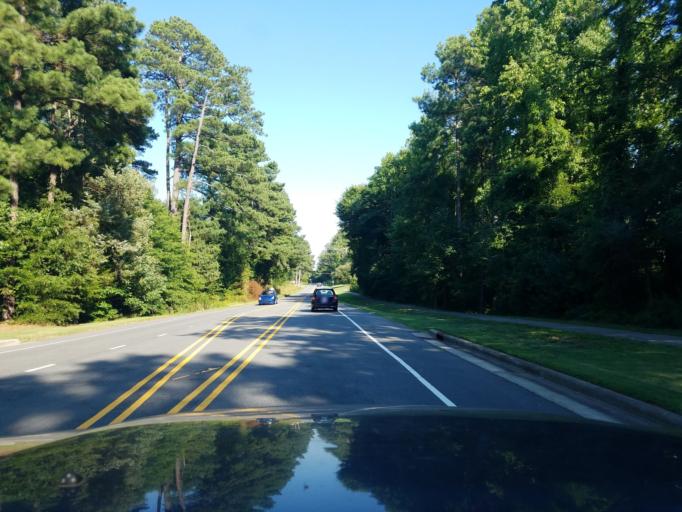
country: US
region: North Carolina
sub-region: Orange County
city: Chapel Hill
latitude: 35.8925
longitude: -79.0013
